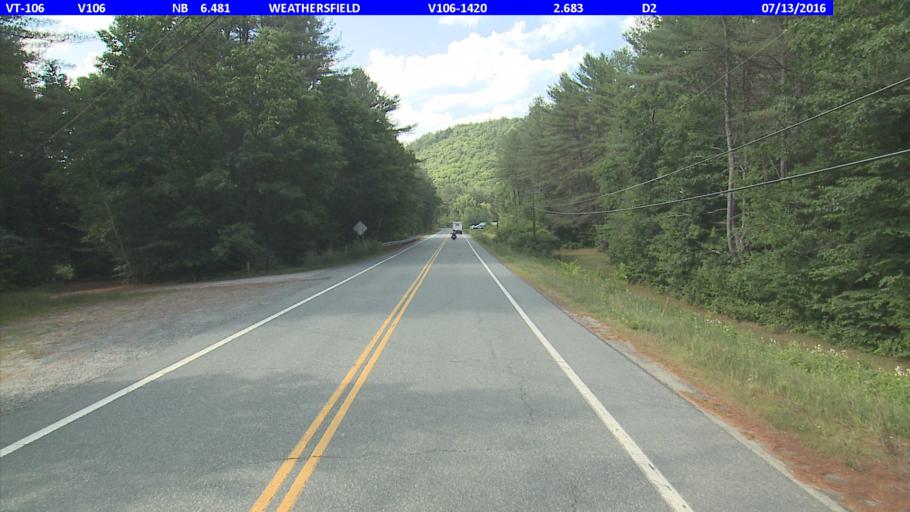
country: US
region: Vermont
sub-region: Windsor County
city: Springfield
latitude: 43.3779
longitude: -72.5085
